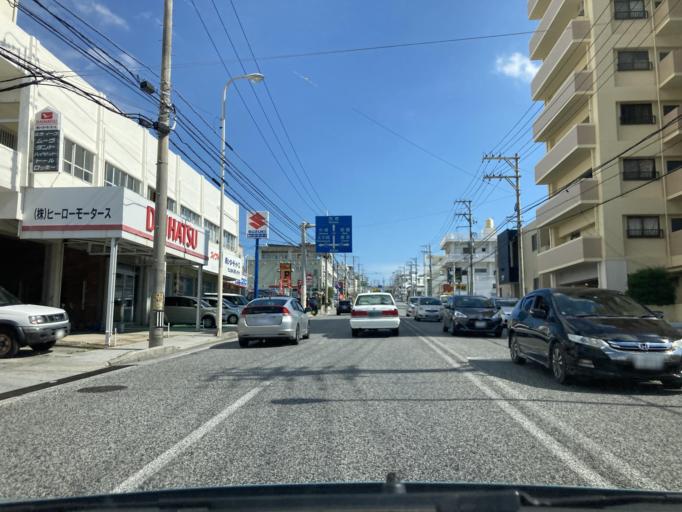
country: JP
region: Okinawa
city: Ginowan
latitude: 26.2578
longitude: 127.7498
